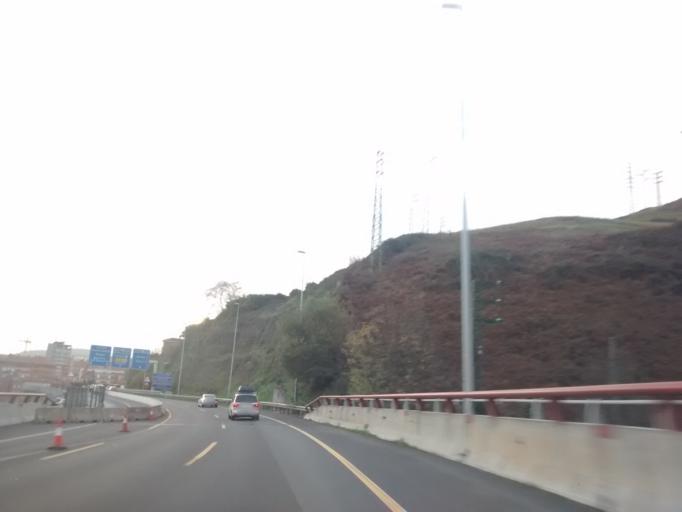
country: ES
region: Basque Country
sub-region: Bizkaia
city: Bilbao
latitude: 43.2565
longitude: -2.9527
